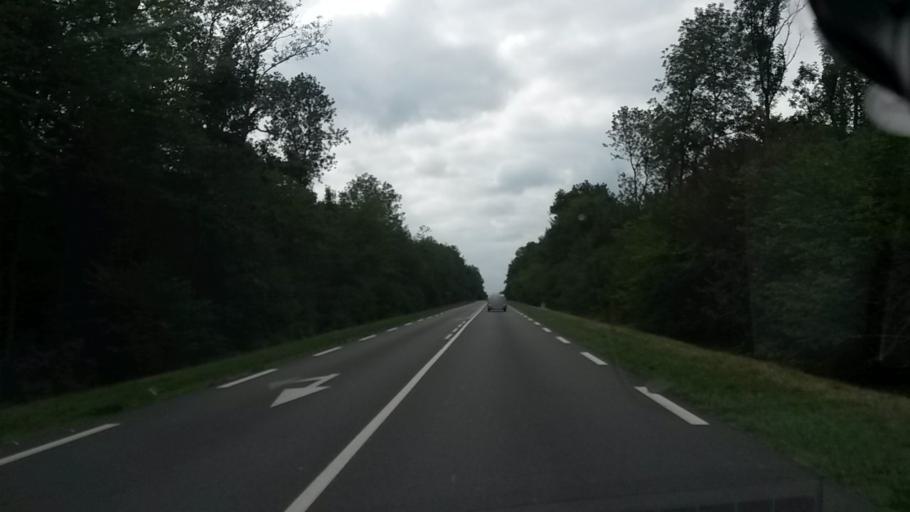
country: FR
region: Picardie
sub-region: Departement de la Somme
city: Camon
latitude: 49.9268
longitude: 2.3893
